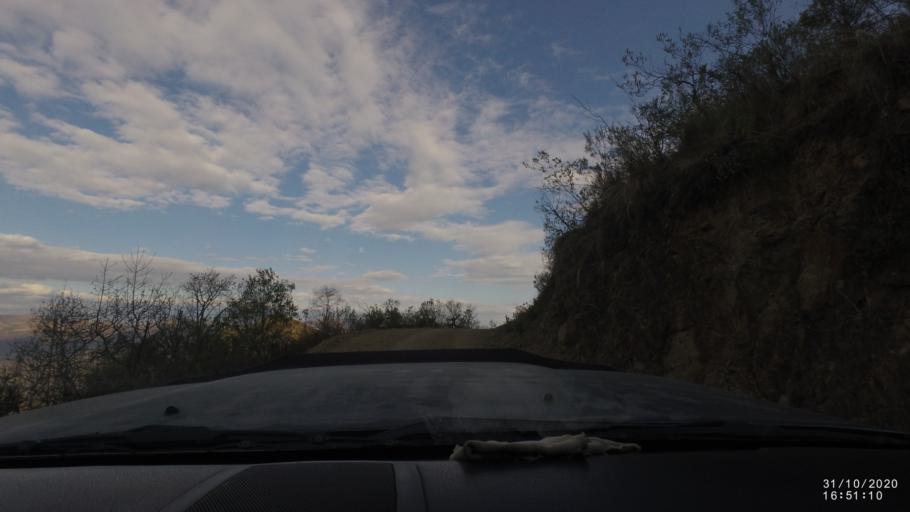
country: BO
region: Chuquisaca
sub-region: Provincia Zudanez
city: Mojocoya
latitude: -18.5110
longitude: -64.5718
